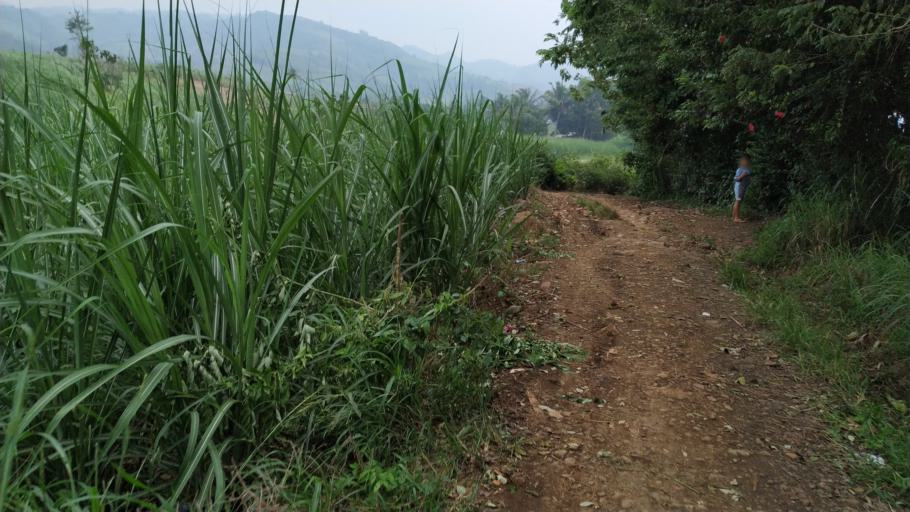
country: PH
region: Western Visayas
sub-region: Province of Negros Occidental
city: Quezon
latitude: 10.4236
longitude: 123.2384
